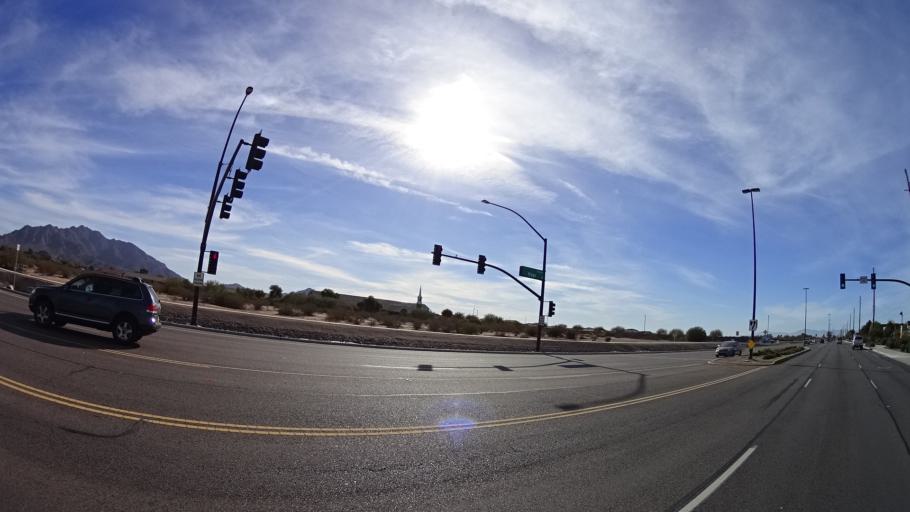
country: US
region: Arizona
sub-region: Maricopa County
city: Queen Creek
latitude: 33.2193
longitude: -111.7273
